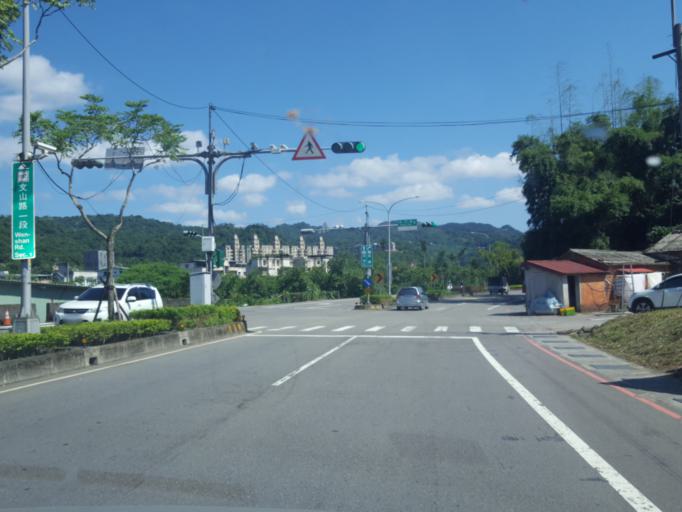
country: TW
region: Taipei
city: Taipei
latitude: 25.0081
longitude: 121.6329
